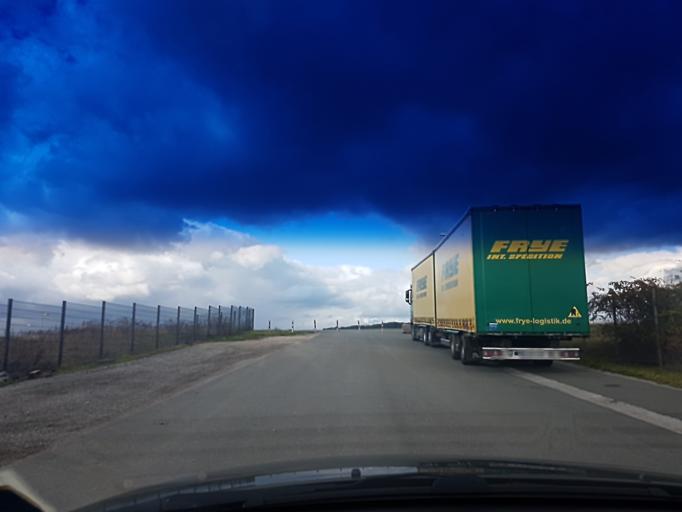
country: DE
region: Bavaria
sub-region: Upper Franconia
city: Schlusselfeld
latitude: 49.7508
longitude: 10.6426
